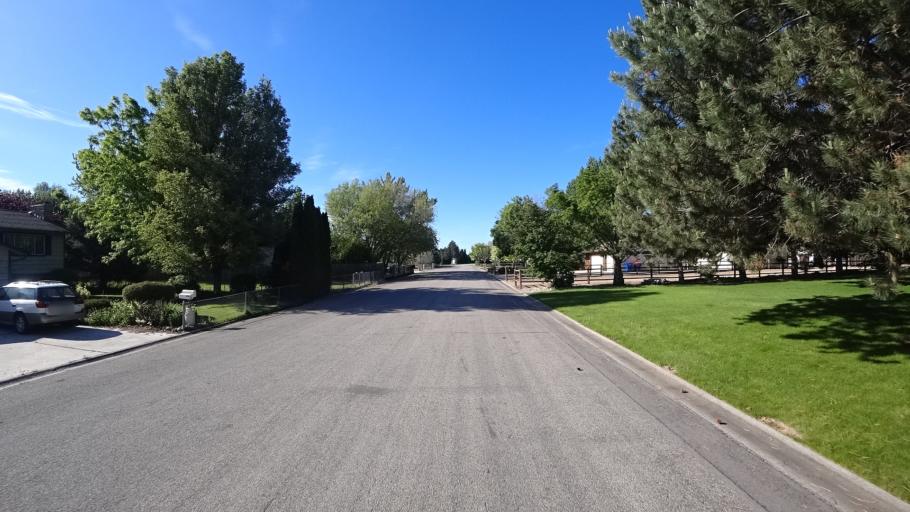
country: US
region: Idaho
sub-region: Ada County
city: Garden City
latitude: 43.5555
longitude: -116.3031
